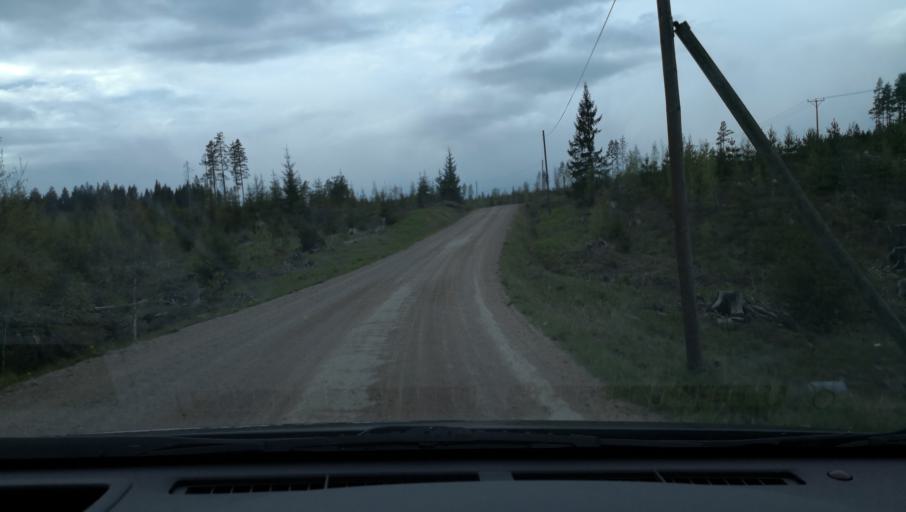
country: SE
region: Vaestmanland
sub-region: Fagersta Kommun
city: Fagersta
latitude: 60.1207
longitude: 15.7770
